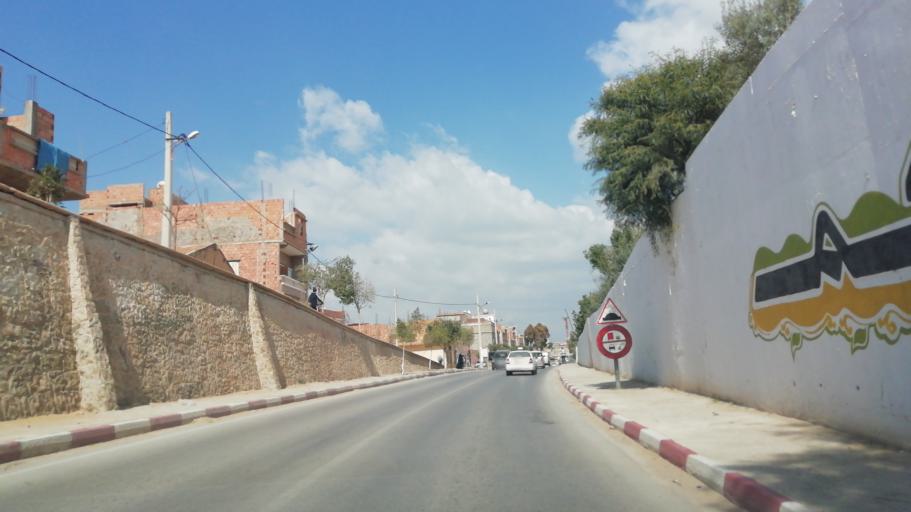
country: DZ
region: Mascara
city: Mascara
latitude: 35.5721
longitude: 0.0689
